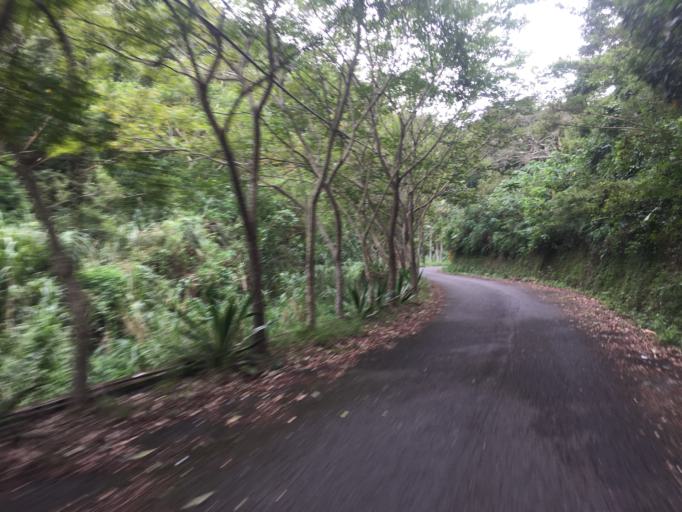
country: TW
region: Taiwan
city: Daxi
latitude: 24.7889
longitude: 121.1627
